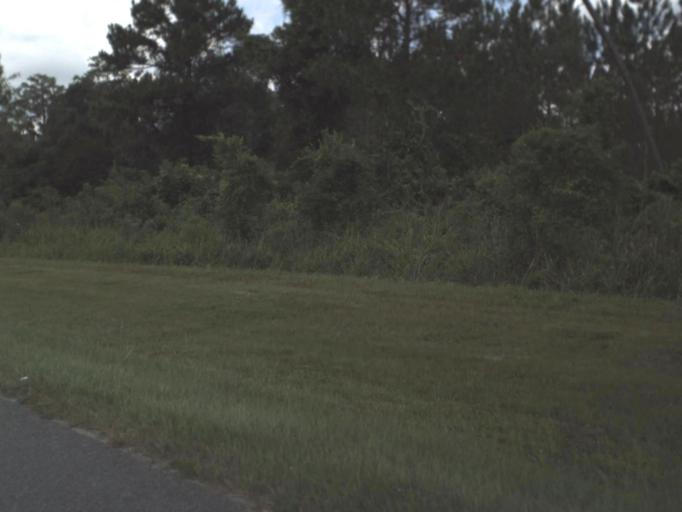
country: US
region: Florida
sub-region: Union County
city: Lake Butler
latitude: 30.0512
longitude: -82.2625
